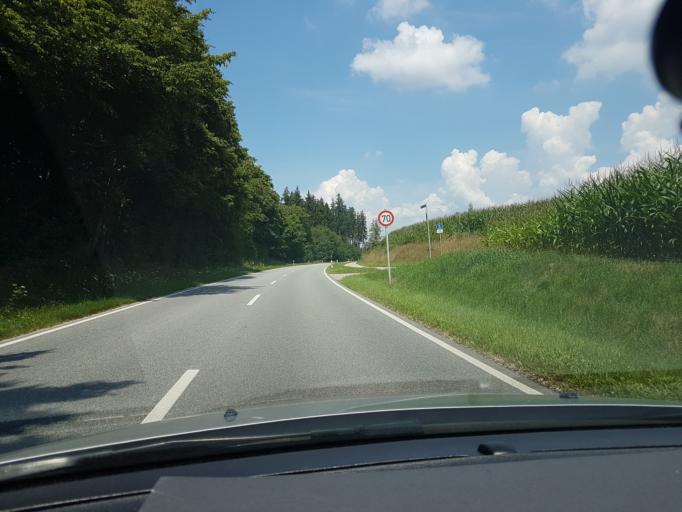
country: DE
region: Bavaria
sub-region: Lower Bavaria
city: Altfraunhofen
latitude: 48.4595
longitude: 12.1656
